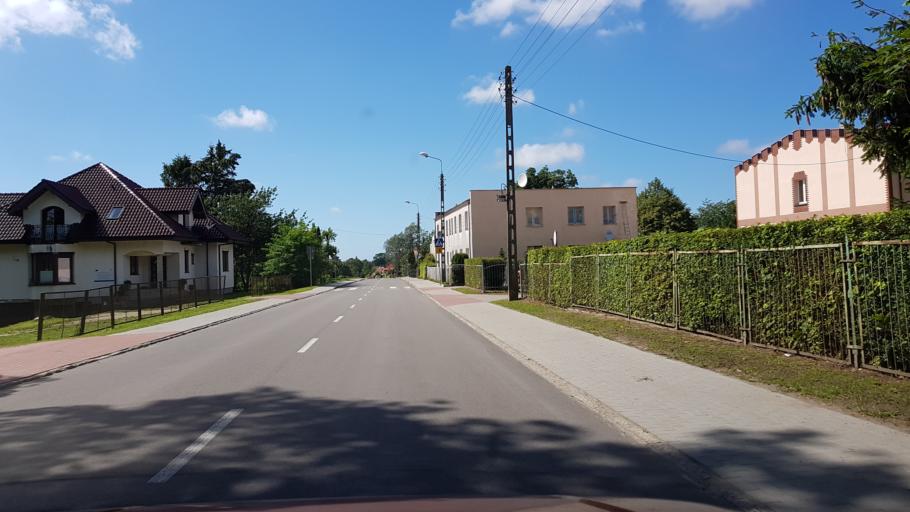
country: PL
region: West Pomeranian Voivodeship
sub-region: Powiat bialogardzki
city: Karlino
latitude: 54.1846
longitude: 15.9222
